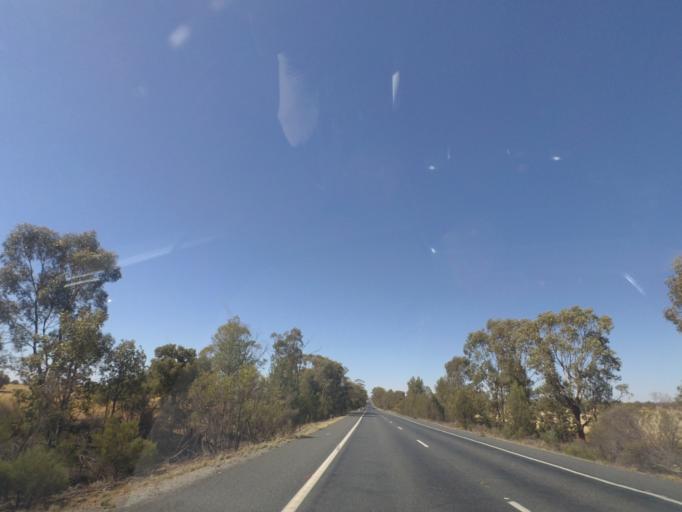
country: AU
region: New South Wales
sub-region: Bland
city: West Wyalong
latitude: -34.1702
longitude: 147.1152
